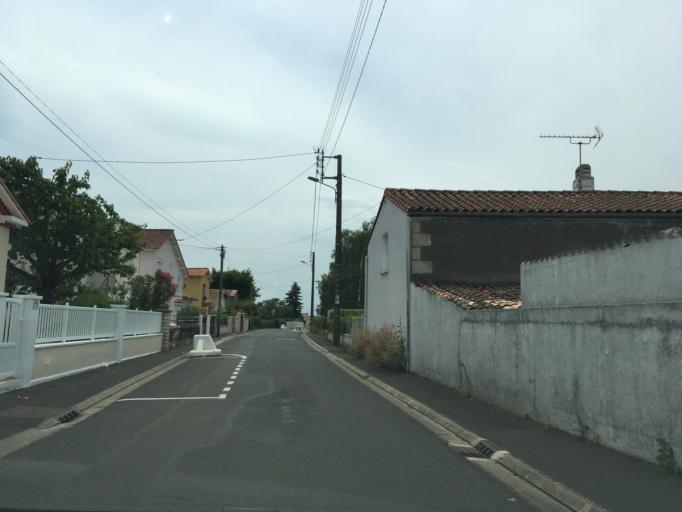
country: FR
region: Poitou-Charentes
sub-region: Departement des Deux-Sevres
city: Niort
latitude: 46.3242
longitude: -0.4852
